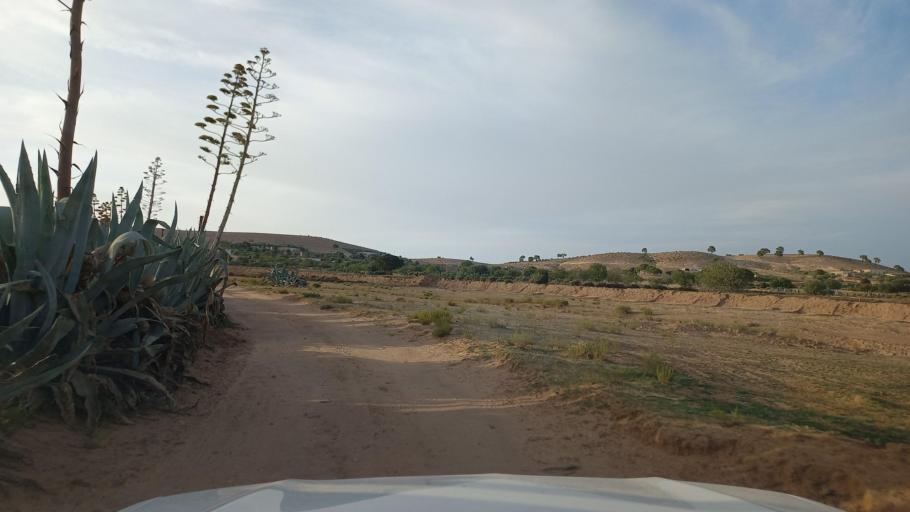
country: TN
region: Al Qasrayn
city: Sbiba
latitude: 35.4077
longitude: 8.9065
